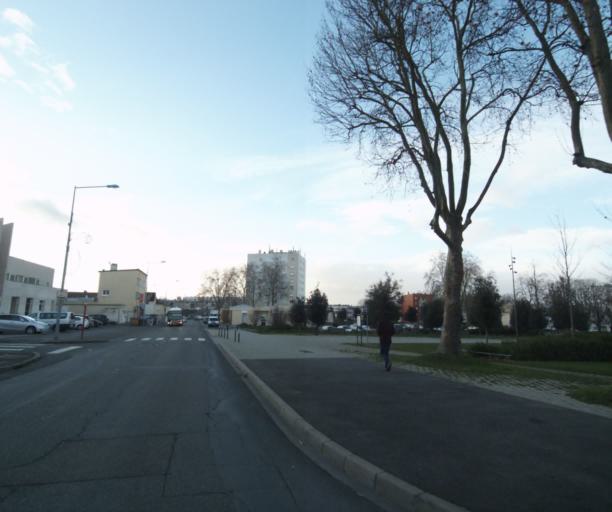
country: FR
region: Pays de la Loire
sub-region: Departement de la Sarthe
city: Le Mans
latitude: 47.9714
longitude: 0.2135
